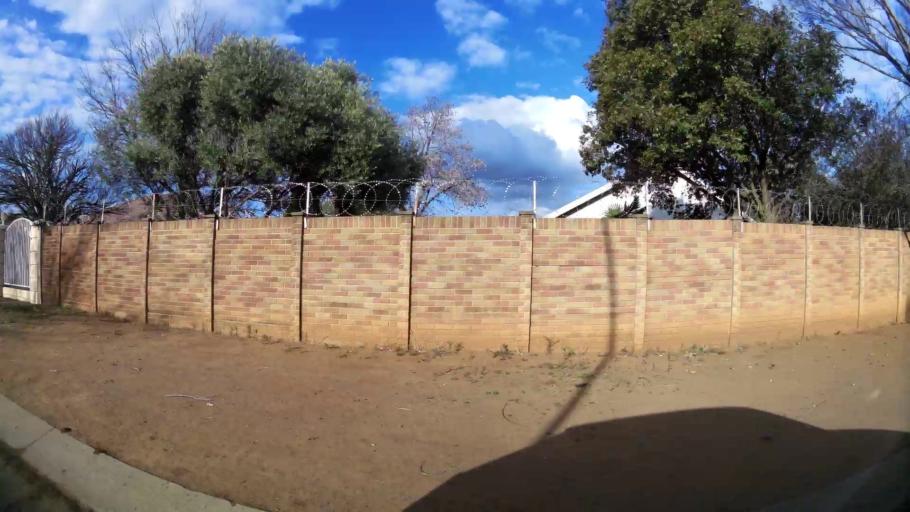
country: ZA
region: Orange Free State
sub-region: Mangaung Metropolitan Municipality
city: Bloemfontein
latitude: -29.1026
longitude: 26.2007
